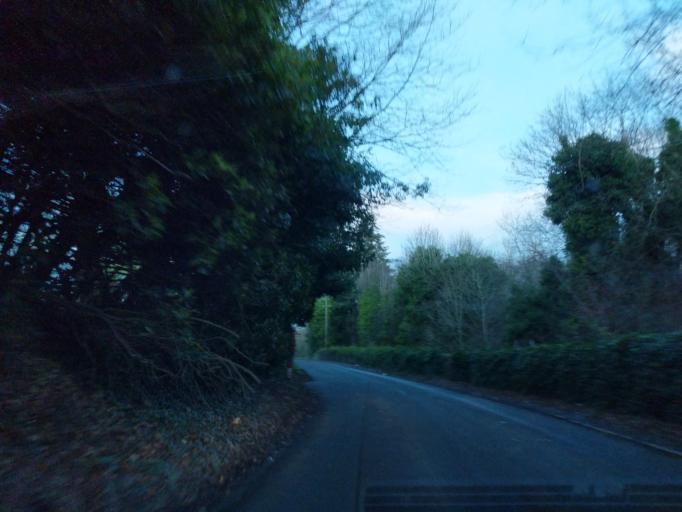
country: GB
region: Scotland
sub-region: Midlothian
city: Bonnyrigg
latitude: 55.8635
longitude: -3.0899
